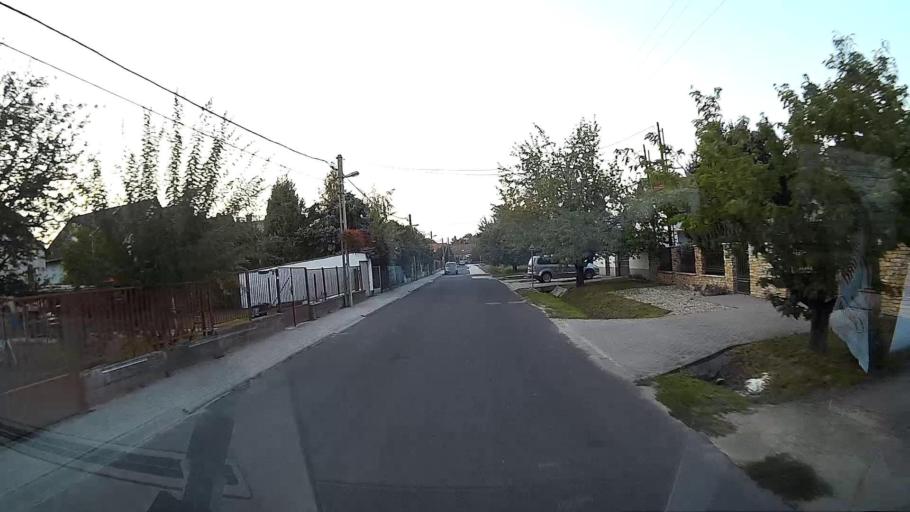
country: HU
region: Pest
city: Budakalasz
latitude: 47.6275
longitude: 19.0521
